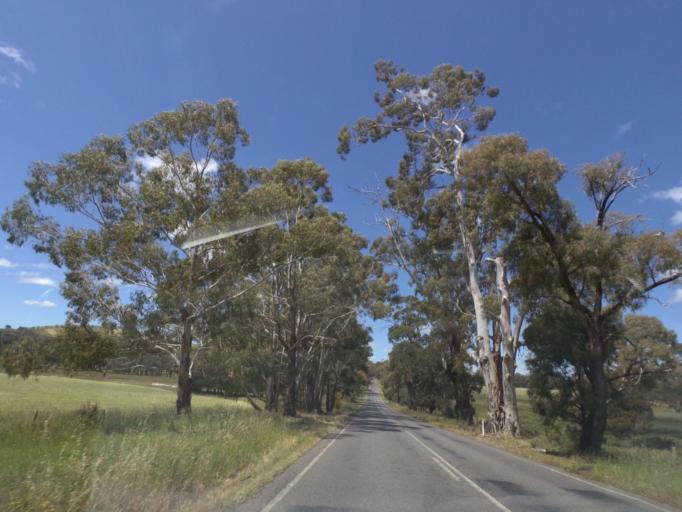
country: AU
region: Victoria
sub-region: Mount Alexander
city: Castlemaine
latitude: -37.3181
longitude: 144.2128
